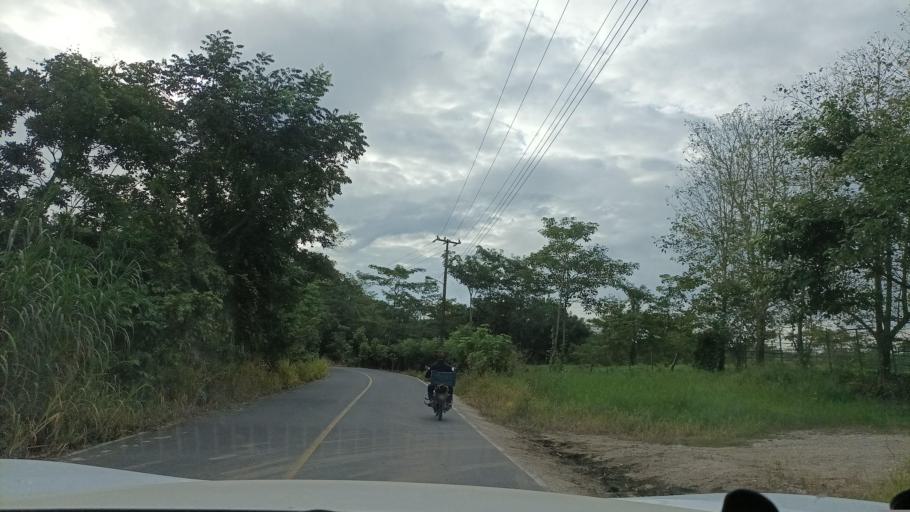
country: MX
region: Veracruz
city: Hidalgotitlan
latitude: 17.7313
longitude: -94.4853
